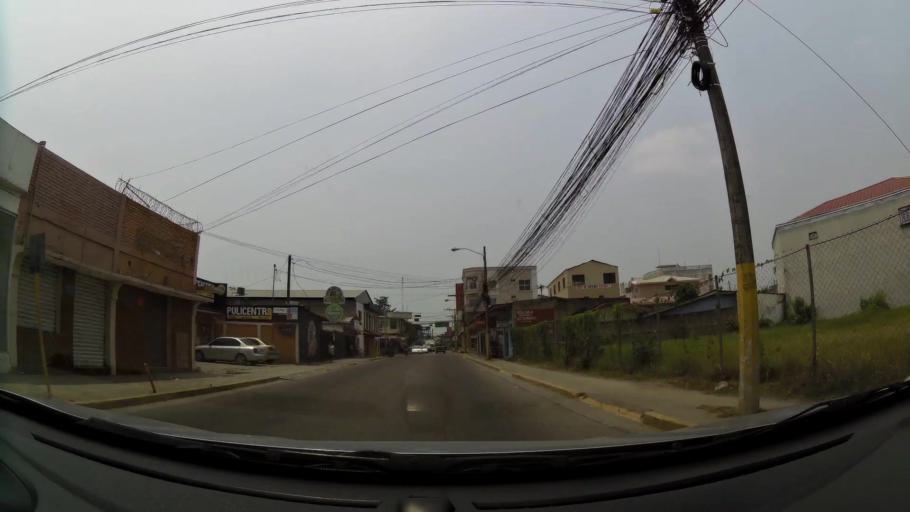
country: HN
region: Yoro
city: El Progreso
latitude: 15.3997
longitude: -87.8096
